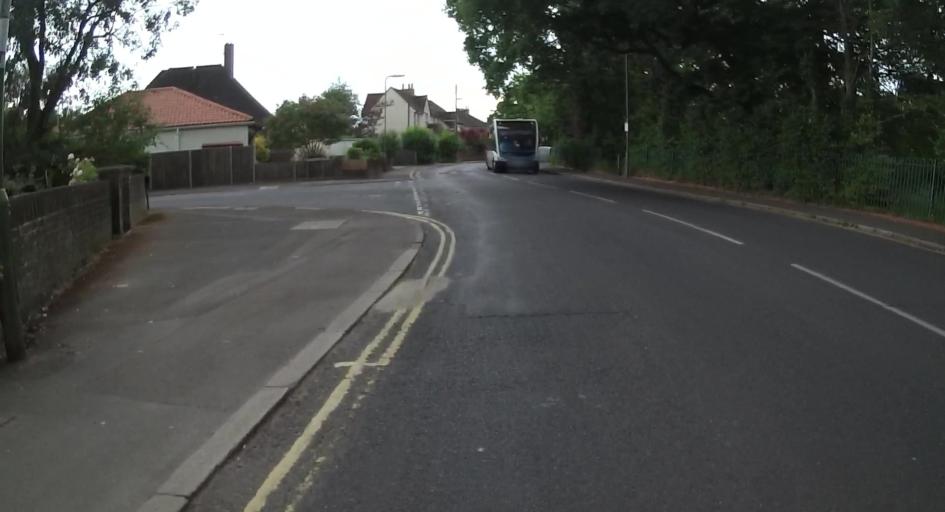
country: GB
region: England
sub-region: Hampshire
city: Aldershot
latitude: 51.2420
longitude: -0.7579
